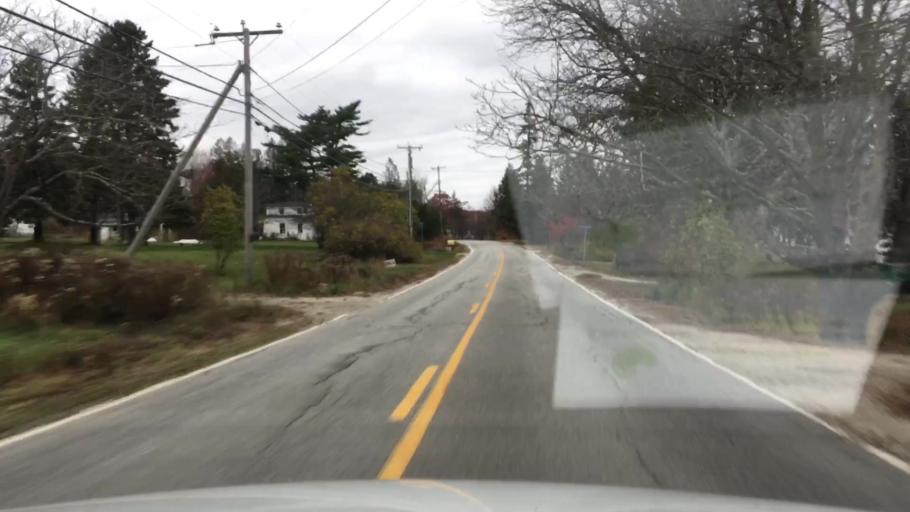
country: US
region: Maine
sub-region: Hancock County
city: Sedgwick
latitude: 44.3603
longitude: -68.5499
